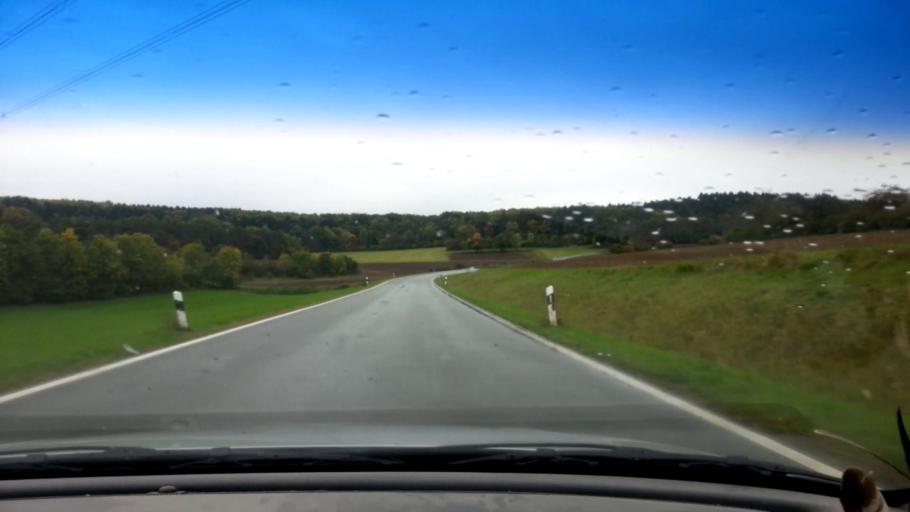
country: DE
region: Bavaria
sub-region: Upper Franconia
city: Poxdorf
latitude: 49.8798
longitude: 11.1055
